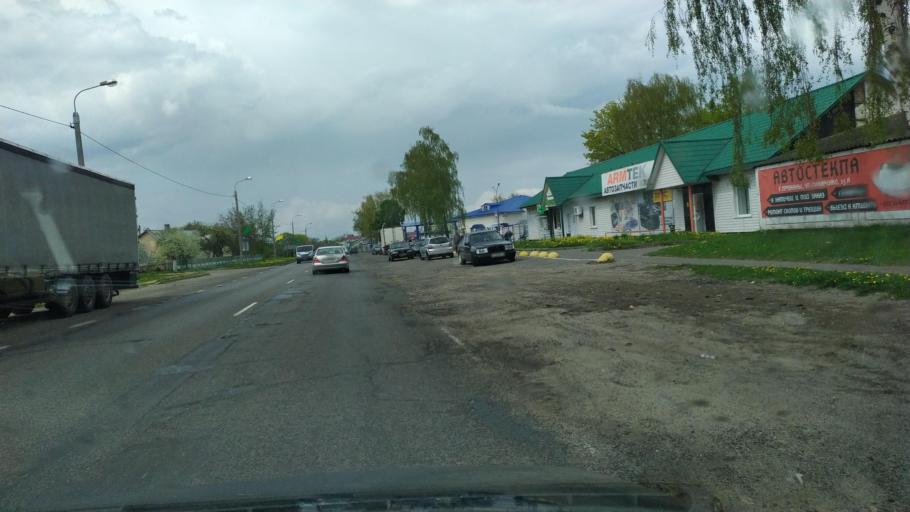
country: BY
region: Brest
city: Pruzhany
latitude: 52.5514
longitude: 24.4781
